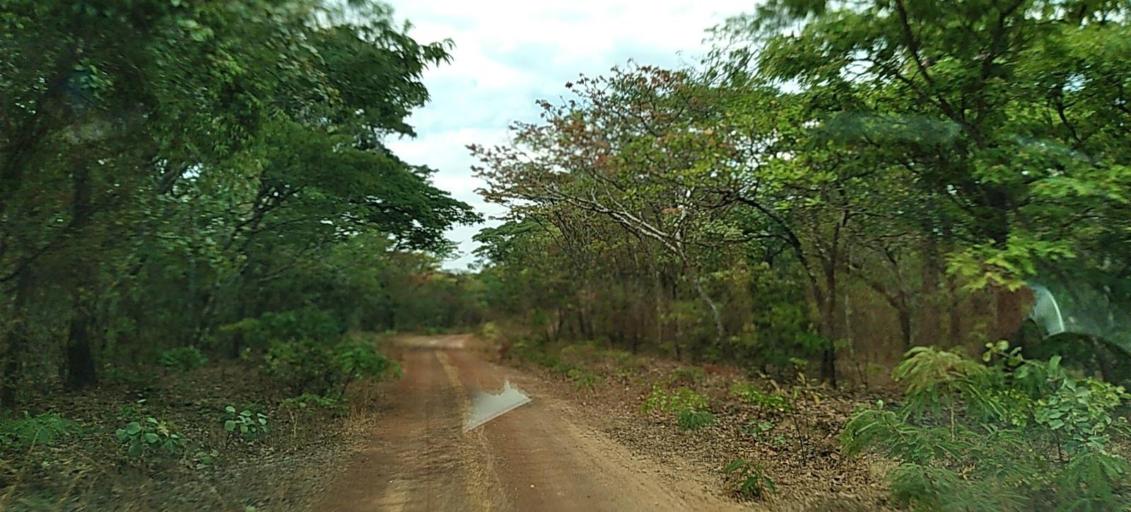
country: ZM
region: Copperbelt
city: Chililabombwe
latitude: -12.4521
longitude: 27.6109
